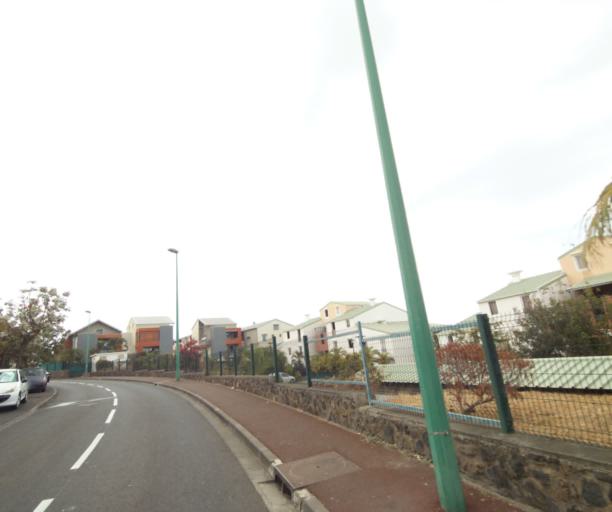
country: RE
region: Reunion
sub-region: Reunion
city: Saint-Paul
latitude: -21.0638
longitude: 55.2290
